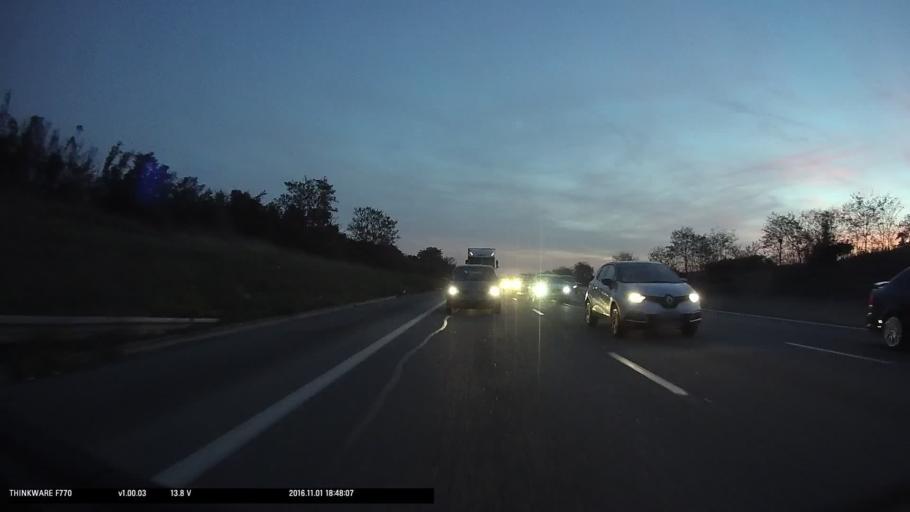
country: FR
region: Ile-de-France
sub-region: Departement de l'Essonne
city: Chilly-Mazarin
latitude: 48.7223
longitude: 2.3119
